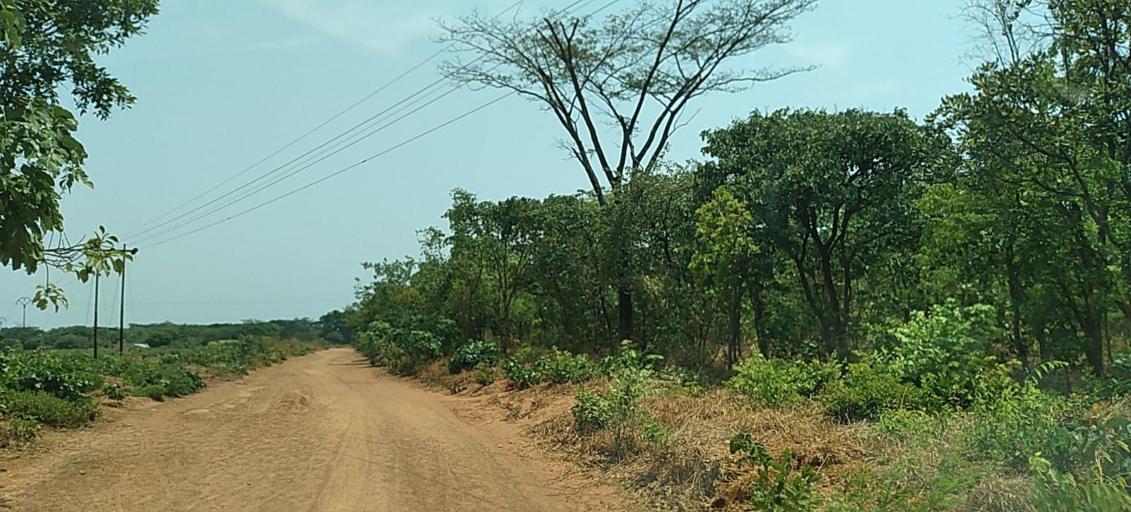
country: ZM
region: Copperbelt
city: Ndola
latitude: -13.0533
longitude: 28.7371
